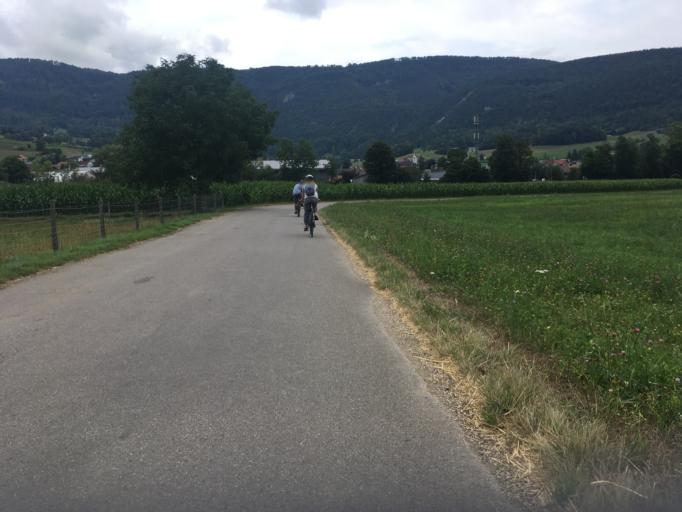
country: CH
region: Solothurn
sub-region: Bezirk Thal
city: Laupersdorf
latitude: 47.3077
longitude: 7.6532
